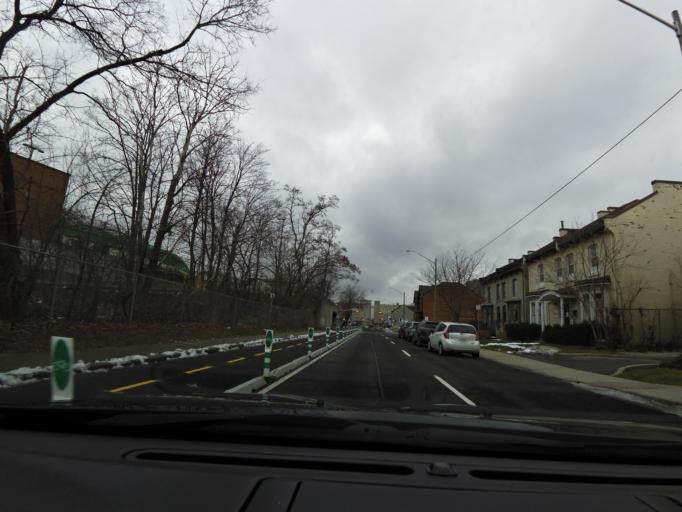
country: CA
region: Ontario
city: Hamilton
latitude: 43.2524
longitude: -79.8654
